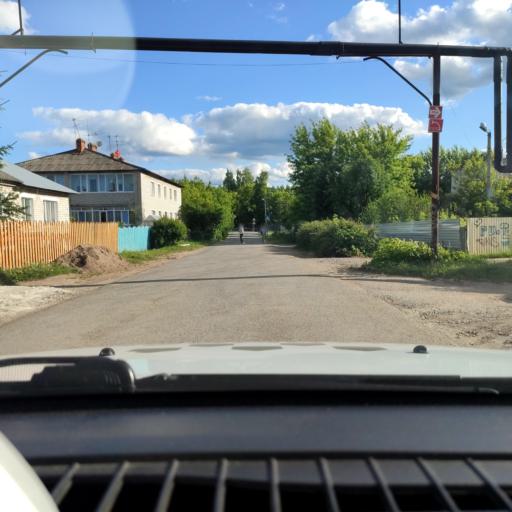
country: RU
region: Perm
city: Ferma
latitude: 57.9040
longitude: 56.3020
